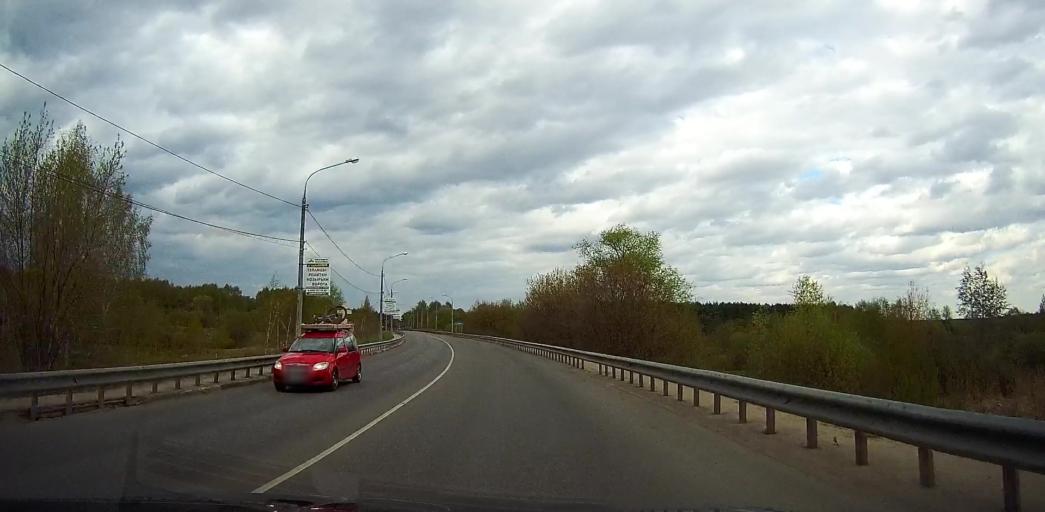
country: RU
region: Moskovskaya
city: Pavlovskiy Posad
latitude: 55.7957
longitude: 38.6531
